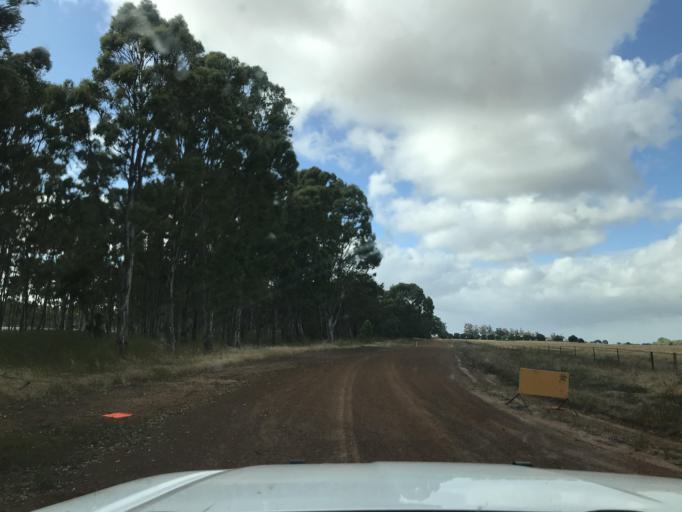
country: AU
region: South Australia
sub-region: Naracoorte and Lucindale
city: Naracoorte
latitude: -36.9481
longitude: 141.4033
